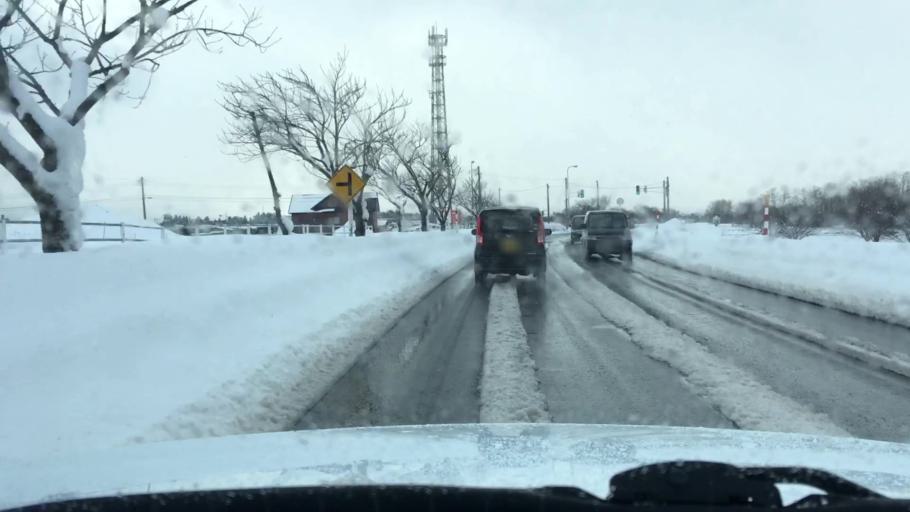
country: JP
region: Aomori
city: Hirosaki
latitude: 40.6226
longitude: 140.4725
